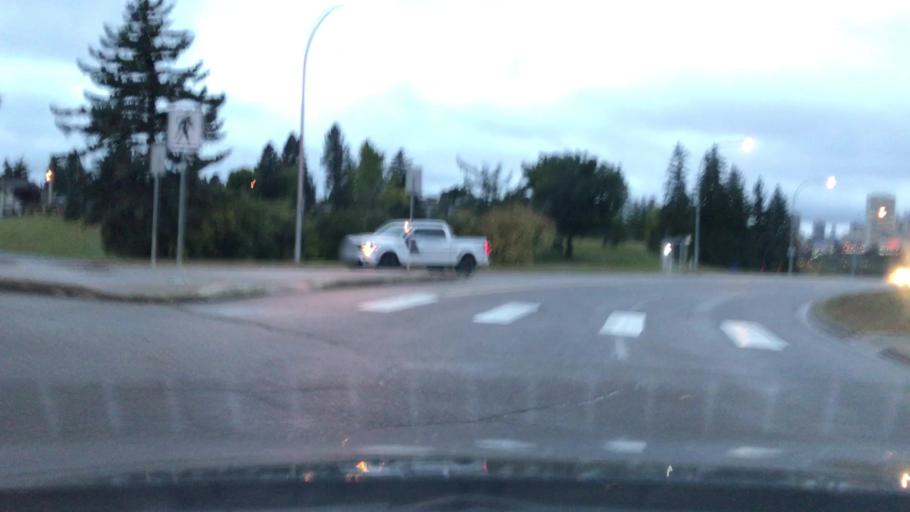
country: CA
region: Alberta
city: Edmonton
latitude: 53.5379
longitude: -113.4568
